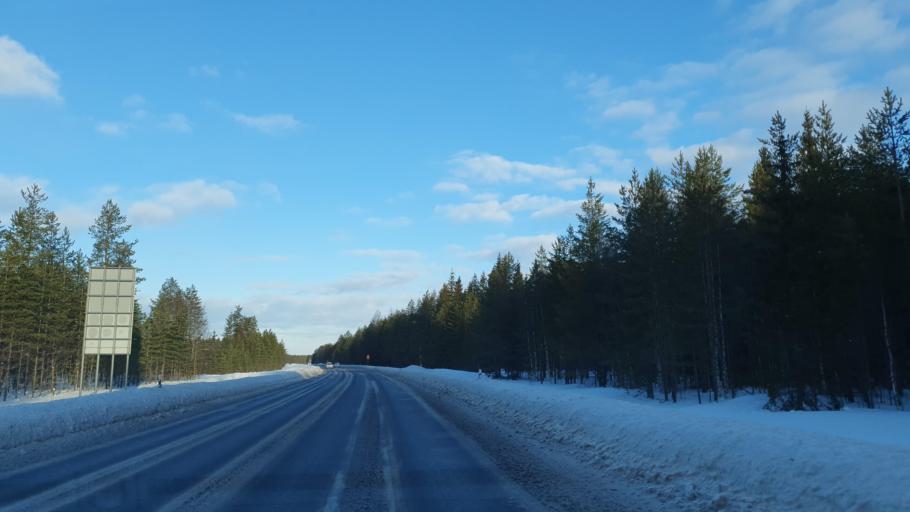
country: FI
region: Northern Ostrobothnia
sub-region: Oulunkaari
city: Utajaervi
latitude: 64.6980
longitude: 26.5335
